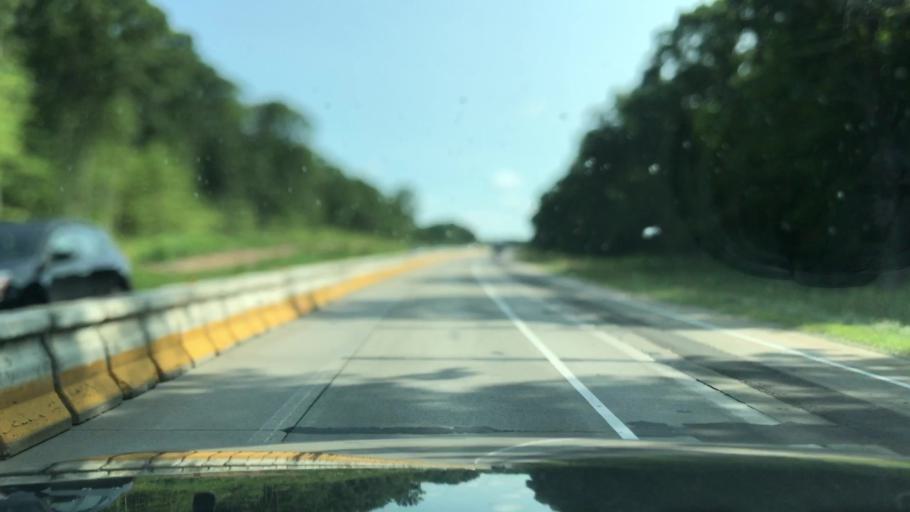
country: US
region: Michigan
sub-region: Kent County
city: Rockford
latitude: 43.1265
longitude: -85.6009
